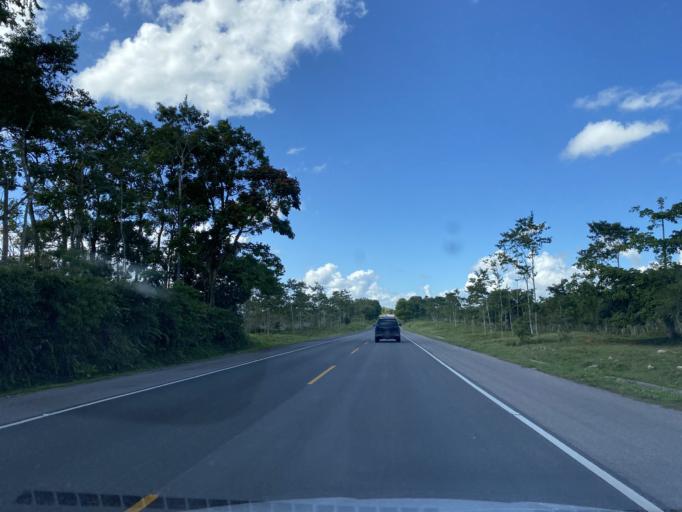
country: DO
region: Monte Plata
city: Sabana Grande de Boya
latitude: 18.9753
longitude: -69.7905
